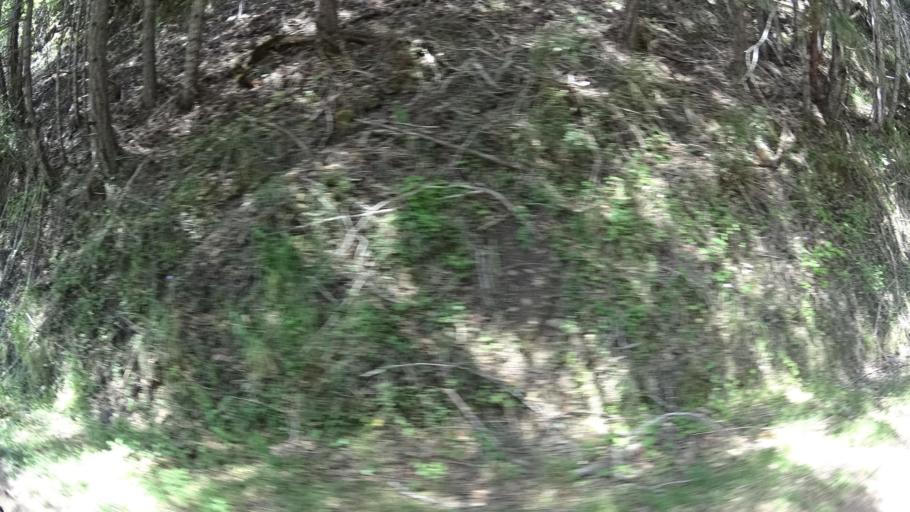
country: US
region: California
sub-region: Humboldt County
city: Redway
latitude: 40.1964
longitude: -123.5260
